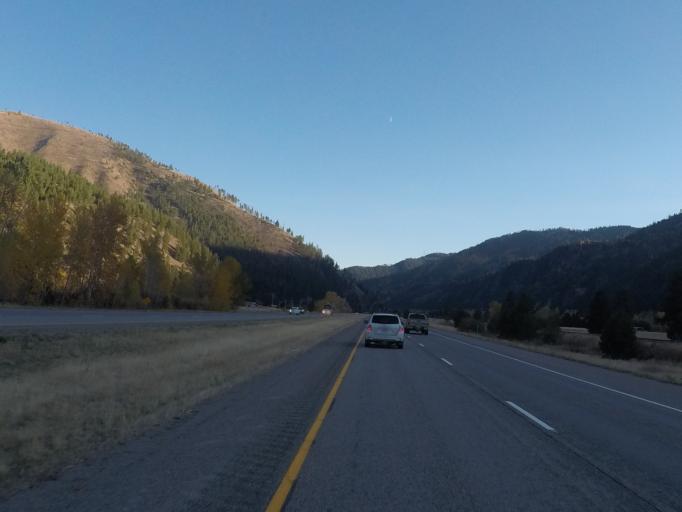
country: US
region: Montana
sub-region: Missoula County
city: Clinton
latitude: 46.7451
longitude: -113.7034
